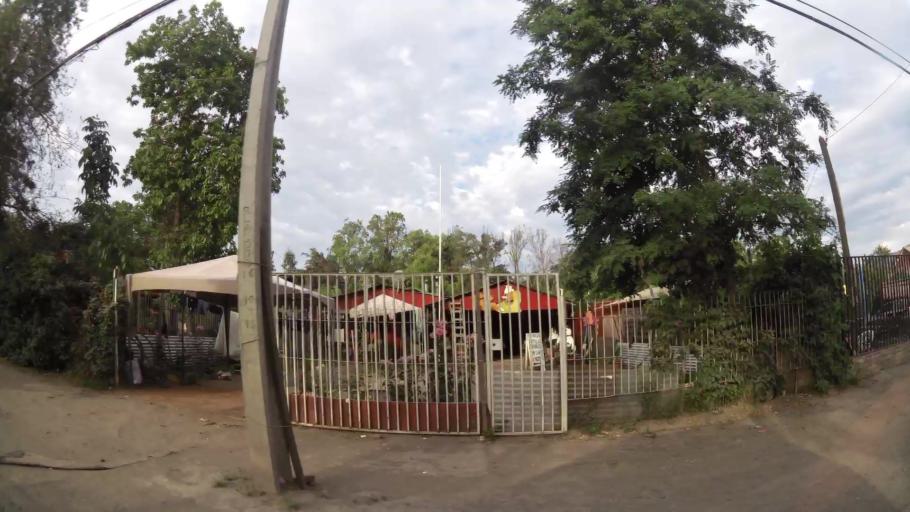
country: CL
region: Santiago Metropolitan
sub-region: Provincia de Maipo
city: San Bernardo
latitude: -33.6444
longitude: -70.6675
